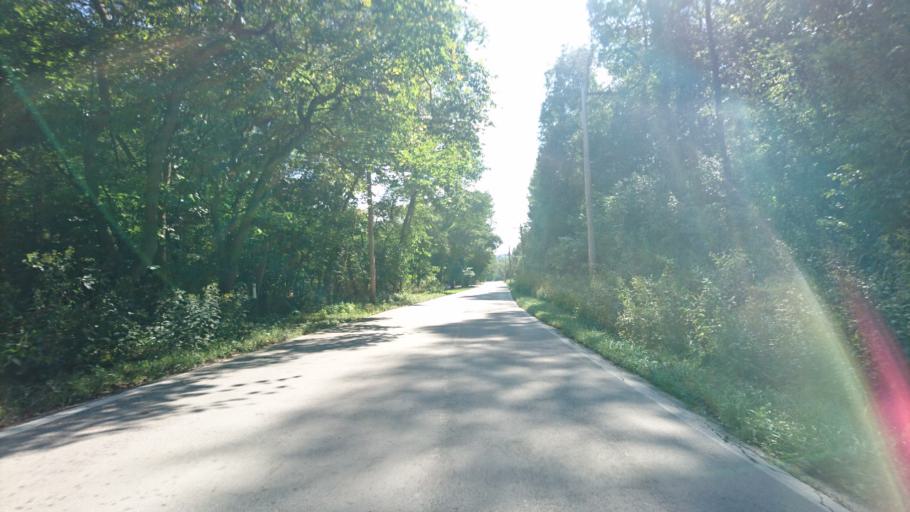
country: US
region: Missouri
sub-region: Saint Louis County
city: Wildwood
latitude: 38.5620
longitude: -90.6389
